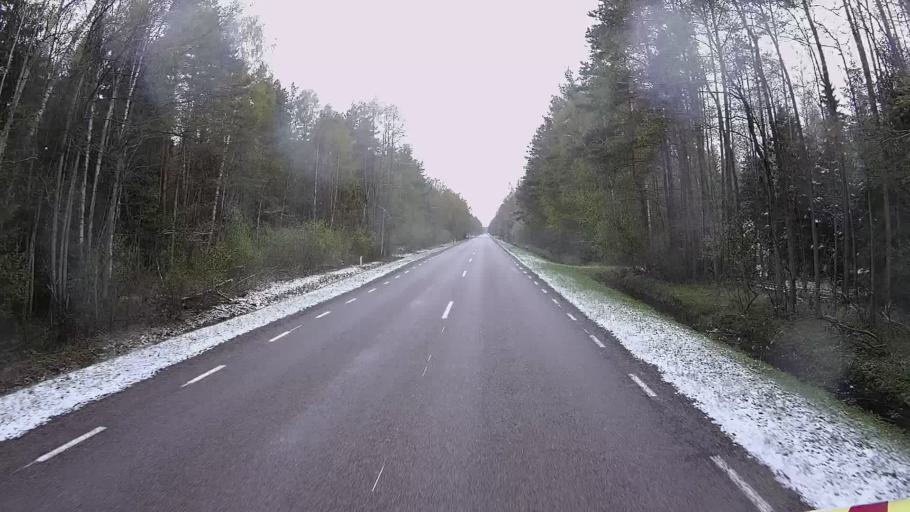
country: EE
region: Hiiumaa
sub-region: Kaerdla linn
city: Kardla
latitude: 58.8411
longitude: 22.4683
